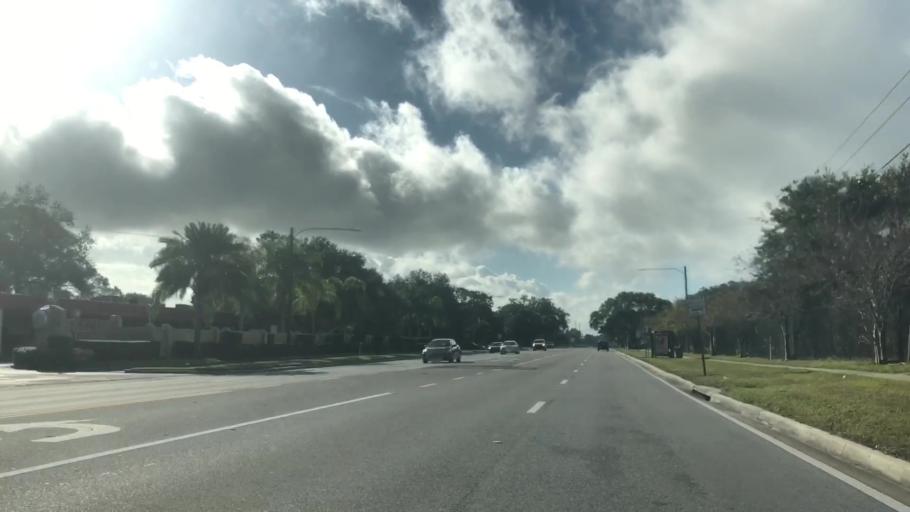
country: US
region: Florida
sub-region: Pinellas County
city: Clearwater
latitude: 27.9728
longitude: -82.7547
